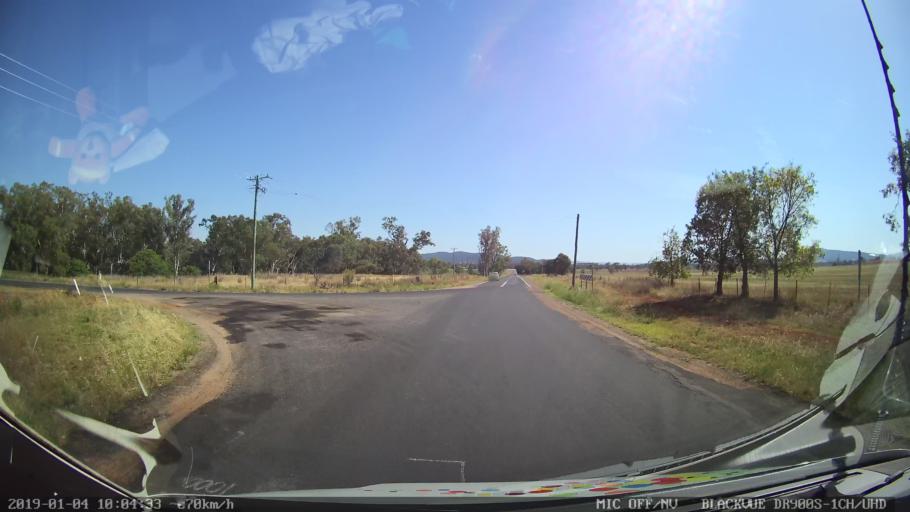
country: AU
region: New South Wales
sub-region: Cabonne
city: Canowindra
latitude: -33.4512
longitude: 148.3615
